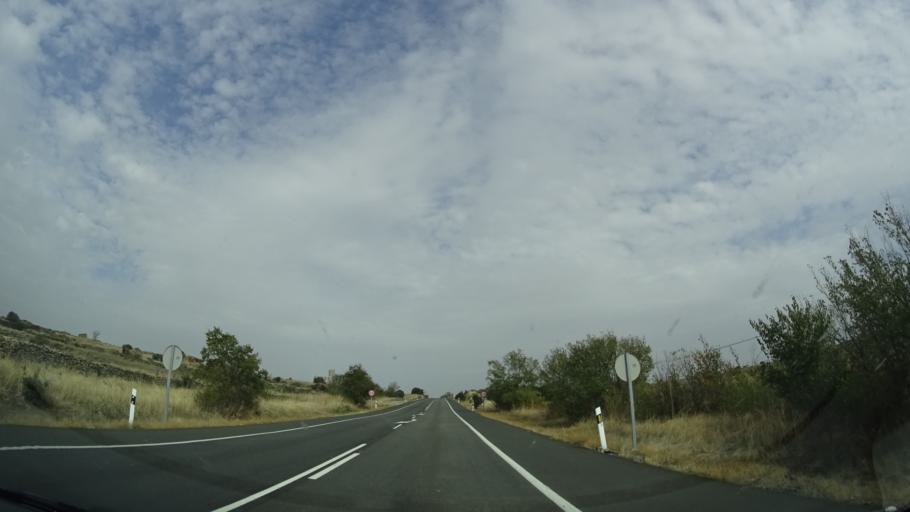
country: ES
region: Extremadura
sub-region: Provincia de Caceres
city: Trujillo
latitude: 39.4441
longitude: -5.8841
